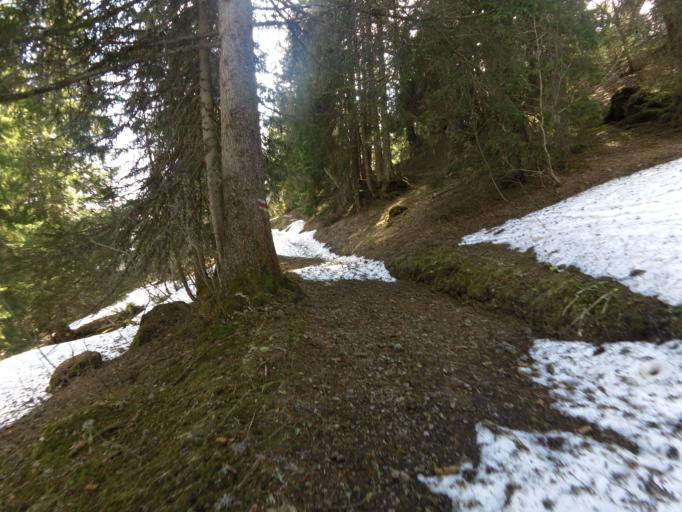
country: CH
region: Nidwalden
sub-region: Nidwalden
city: Emmetten
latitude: 46.8972
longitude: 8.4945
